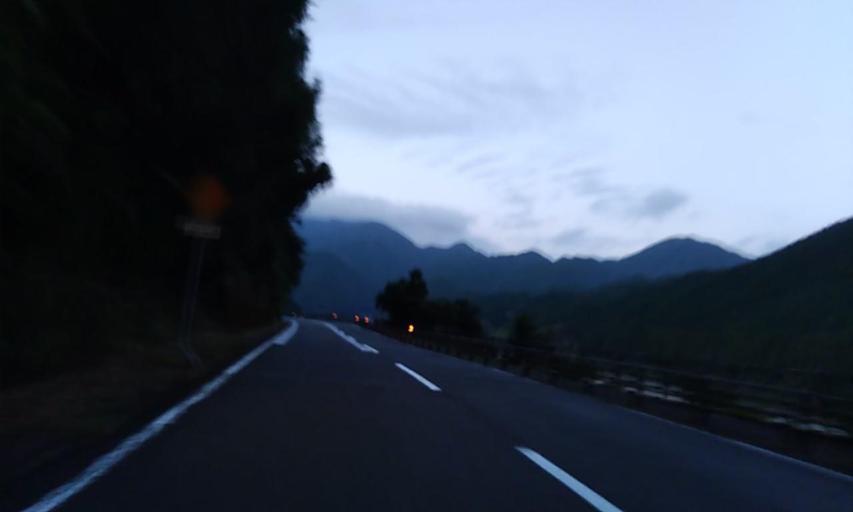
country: JP
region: Wakayama
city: Shingu
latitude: 33.7415
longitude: 135.9386
